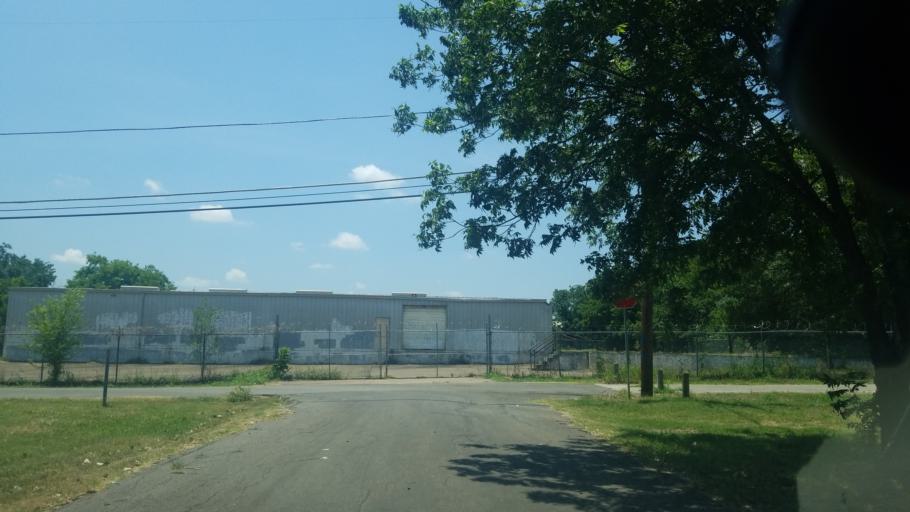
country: US
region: Texas
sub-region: Dallas County
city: Dallas
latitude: 32.7392
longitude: -96.7850
